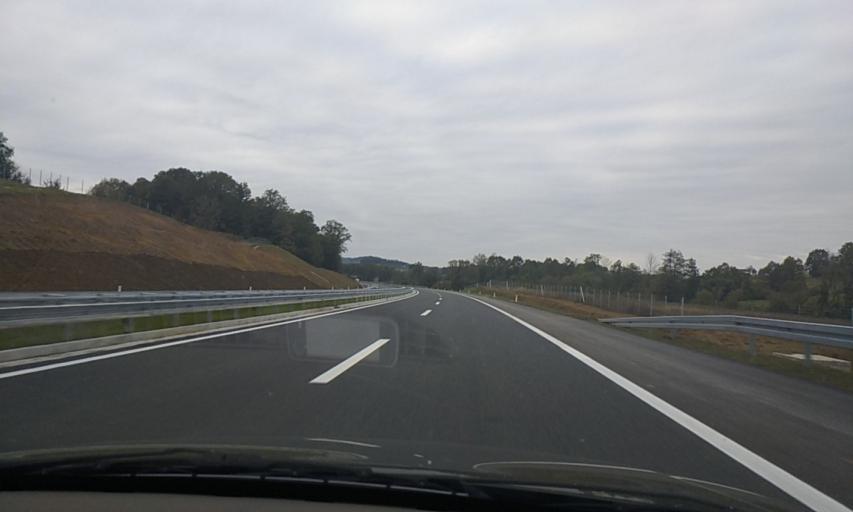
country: BA
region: Republika Srpska
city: Maglajani
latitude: 44.8615
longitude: 17.4771
